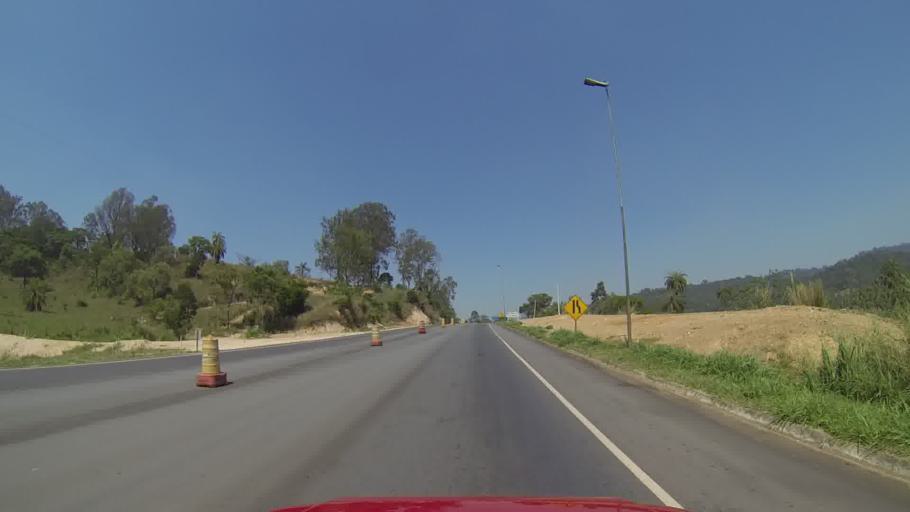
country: BR
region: Minas Gerais
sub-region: Mateus Leme
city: Mateus Leme
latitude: -20.0196
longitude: -44.4965
